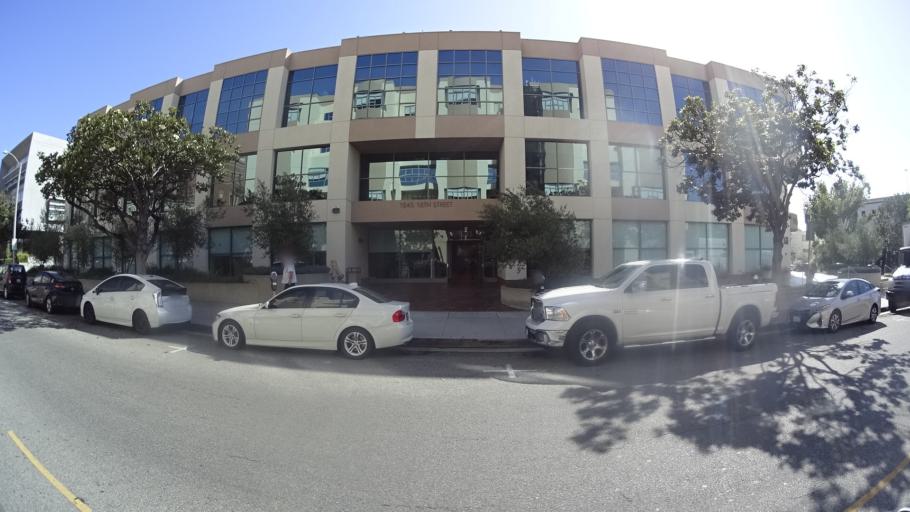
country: US
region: California
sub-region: Los Angeles County
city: Santa Monica
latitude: 34.0273
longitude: -118.4858
